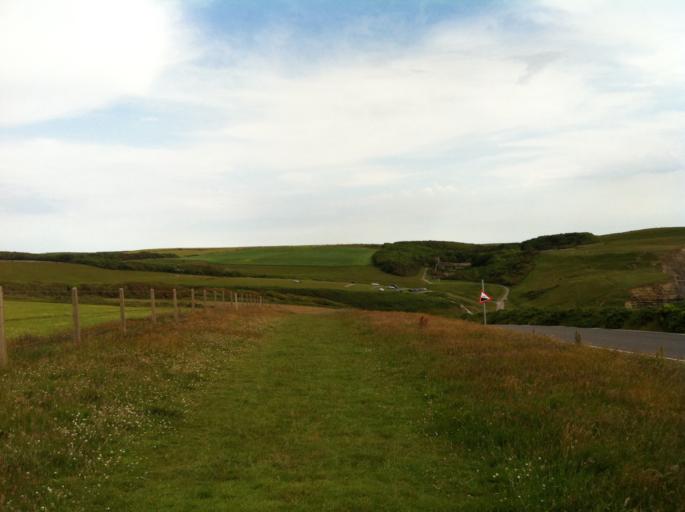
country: GB
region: Wales
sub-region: Bridgend county borough
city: Merthyr Mawr
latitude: 51.4478
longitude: -3.6083
